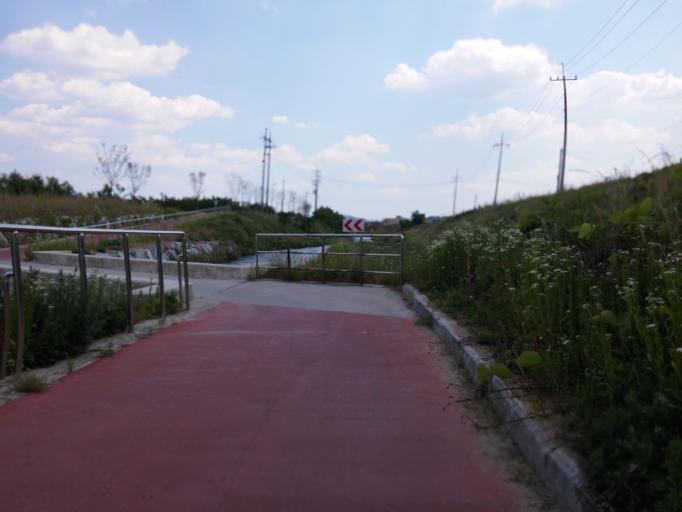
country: KR
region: Chungcheongbuk-do
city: Cheongju-si
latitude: 36.5928
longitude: 127.4966
